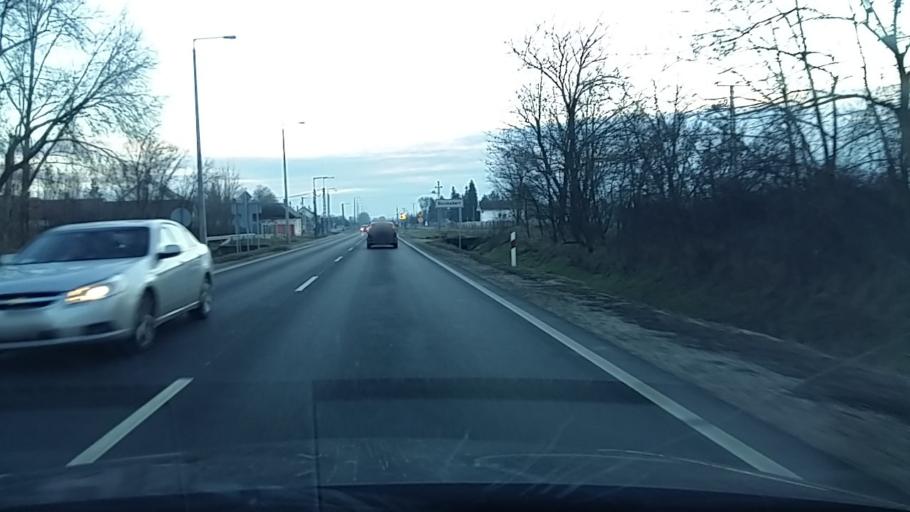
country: HU
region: Hajdu-Bihar
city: Hajduhadhaz
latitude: 47.6502
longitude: 21.6607
